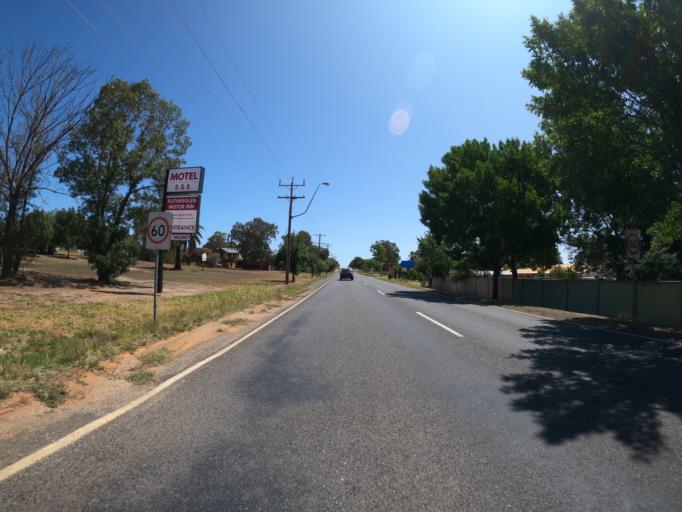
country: AU
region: New South Wales
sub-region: Corowa Shire
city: Corowa
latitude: -36.0524
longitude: 146.4525
